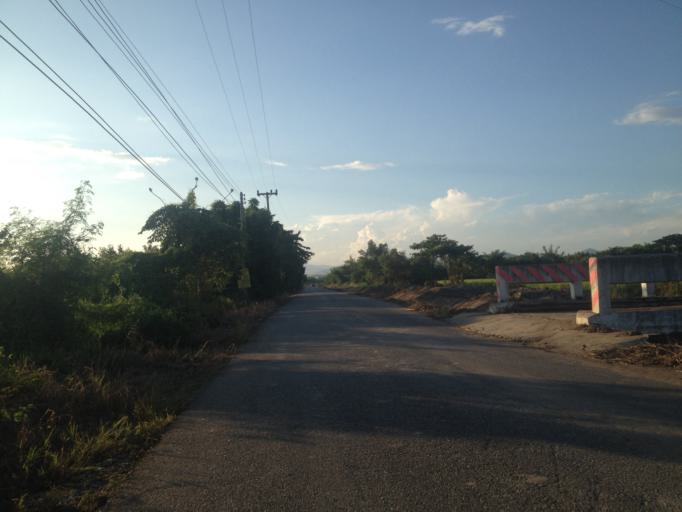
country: TH
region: Chiang Mai
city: San Pa Tong
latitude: 18.6464
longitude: 98.8973
